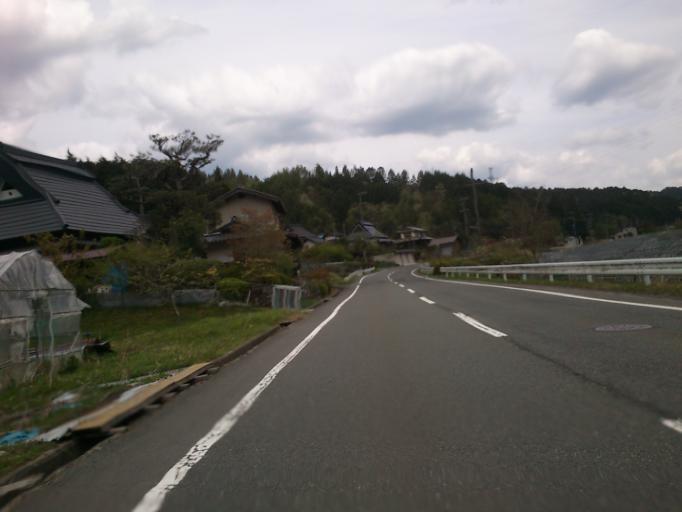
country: JP
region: Kyoto
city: Kameoka
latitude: 35.2068
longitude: 135.5928
